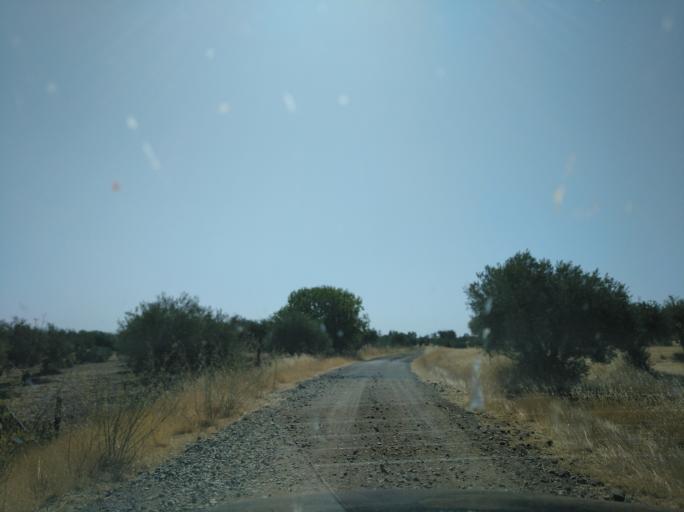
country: PT
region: Portalegre
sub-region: Campo Maior
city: Campo Maior
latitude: 39.0706
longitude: -7.0166
